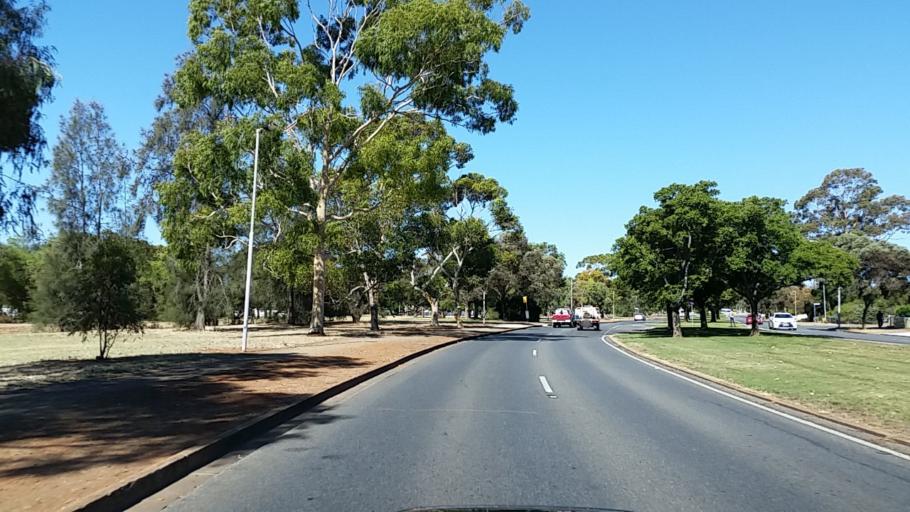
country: AU
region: South Australia
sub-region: Salisbury
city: Elizabeth
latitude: -34.7072
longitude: 138.6864
